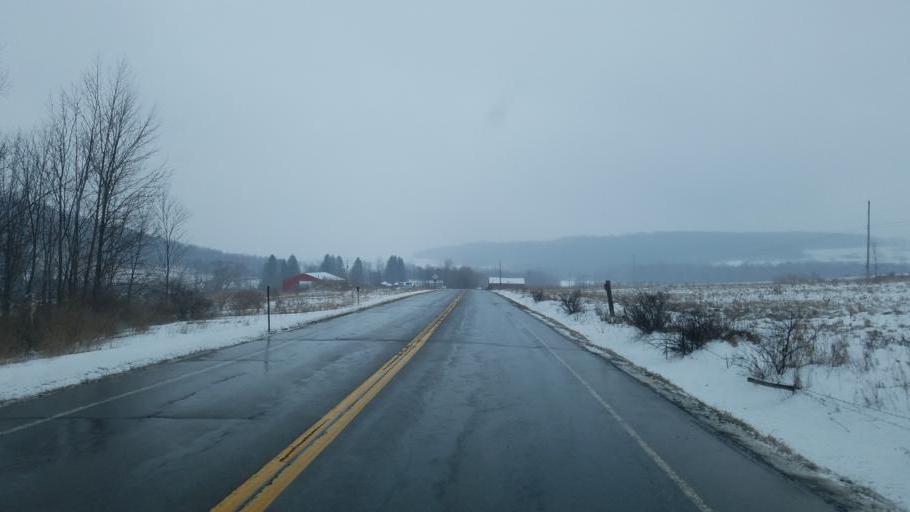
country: US
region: New York
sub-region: Steuben County
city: Canisteo
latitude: 42.1199
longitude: -77.5437
